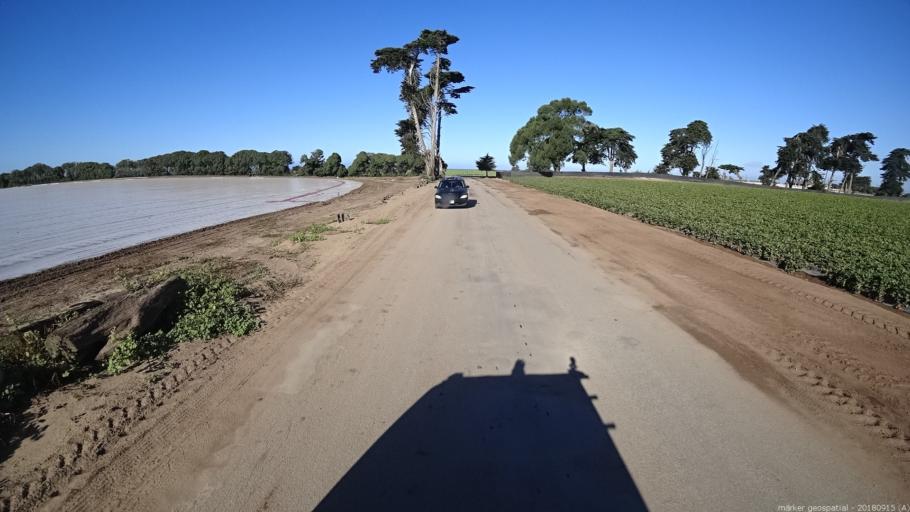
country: US
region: California
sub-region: Monterey County
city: Elkhorn
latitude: 36.8270
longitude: -121.7880
